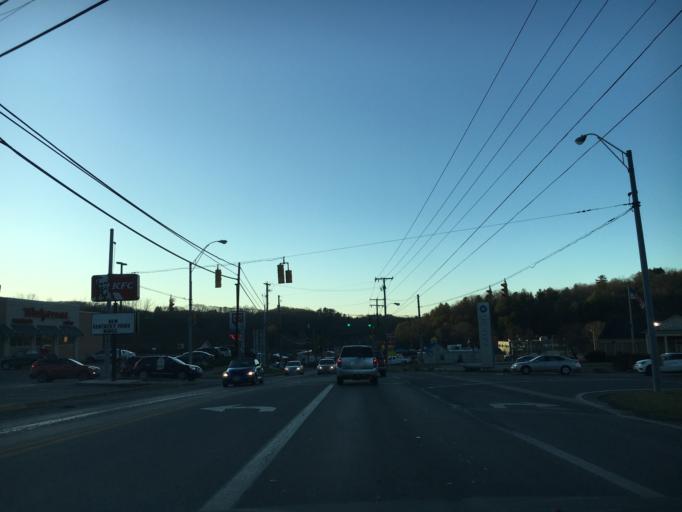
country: US
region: West Virginia
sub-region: Raleigh County
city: Beaver
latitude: 37.7489
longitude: -81.1342
